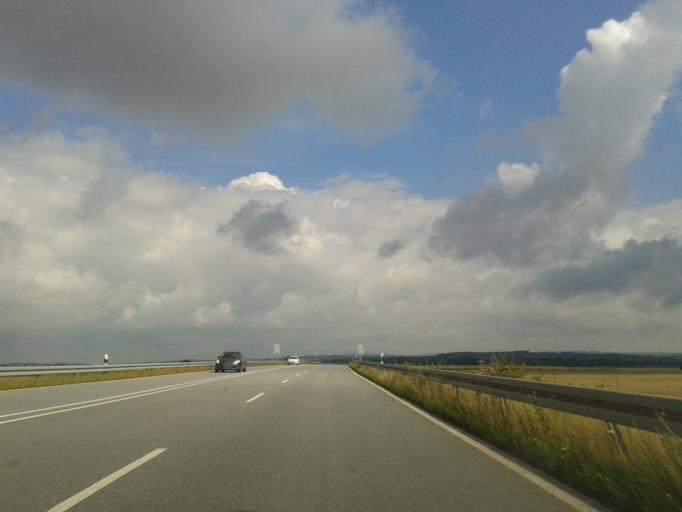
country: DE
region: Saxony
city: Radeberg
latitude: 51.0888
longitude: 13.9376
